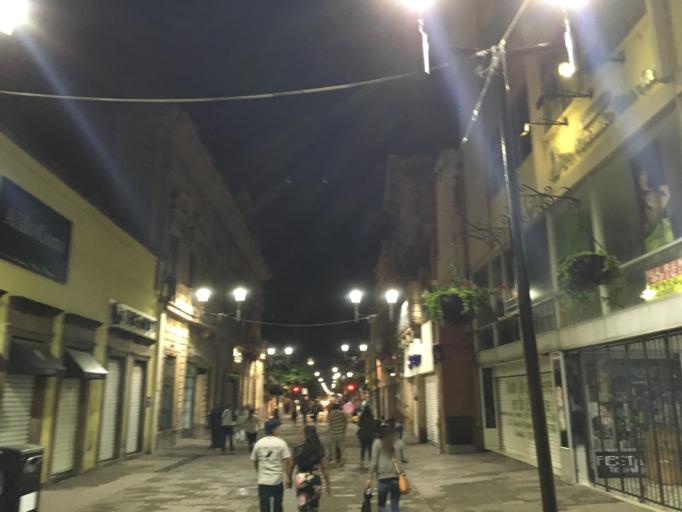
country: MX
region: Guanajuato
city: Leon
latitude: 21.1219
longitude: -101.6815
